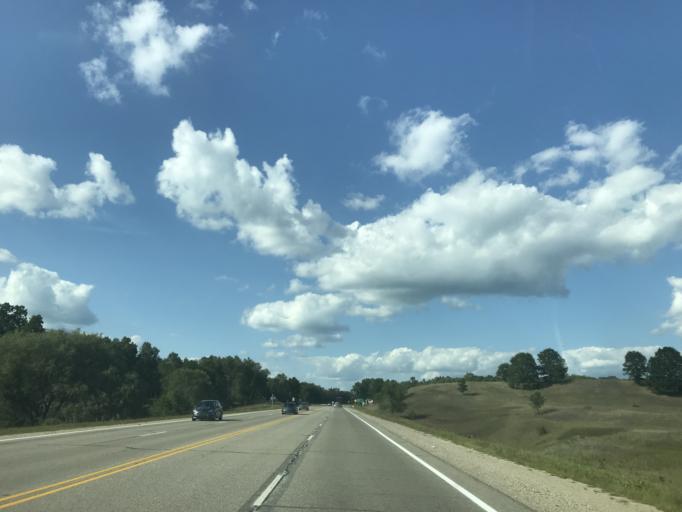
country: US
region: Michigan
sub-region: Newaygo County
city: Newaygo
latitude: 43.4275
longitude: -85.7964
